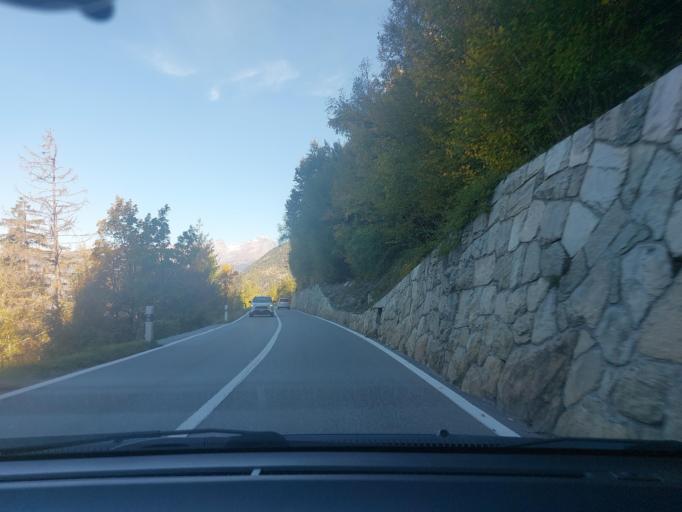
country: CH
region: Valais
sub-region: Sierre District
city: Chippis
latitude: 46.2441
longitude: 7.5767
